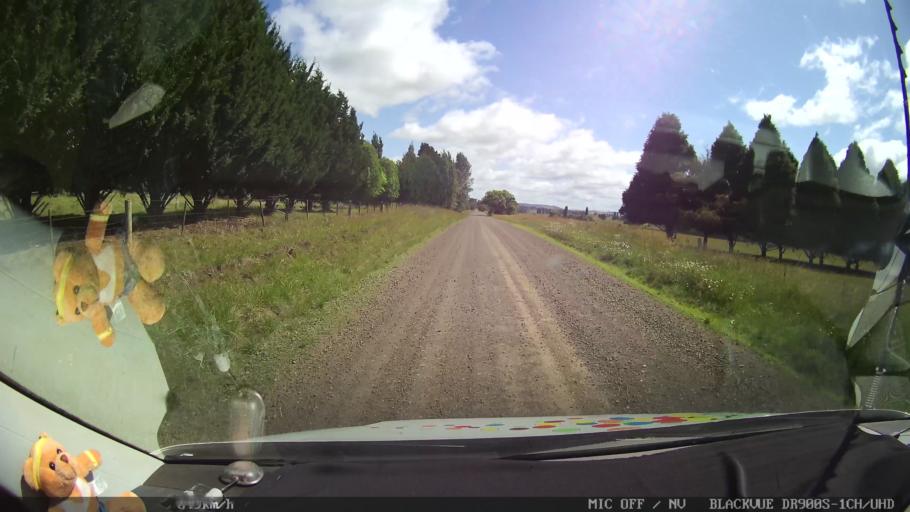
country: AU
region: New South Wales
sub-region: Glen Innes Severn
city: Glen Innes
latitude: -29.9607
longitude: 151.7008
